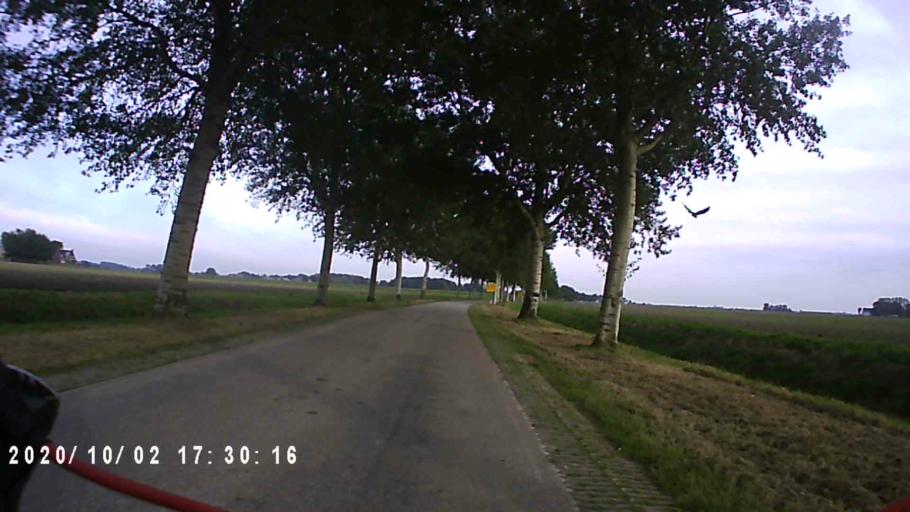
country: NL
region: Groningen
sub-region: Gemeente De Marne
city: Ulrum
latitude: 53.3373
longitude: 6.3264
